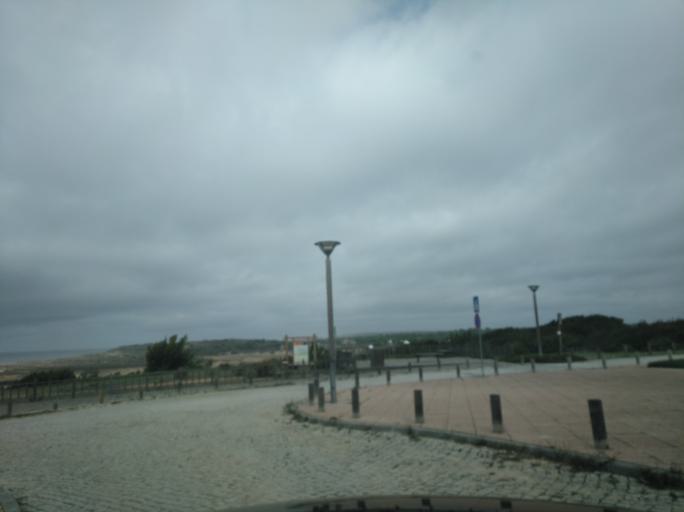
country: PT
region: Setubal
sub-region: Santiago do Cacem
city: Santo Andre
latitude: 38.1288
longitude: -8.7893
